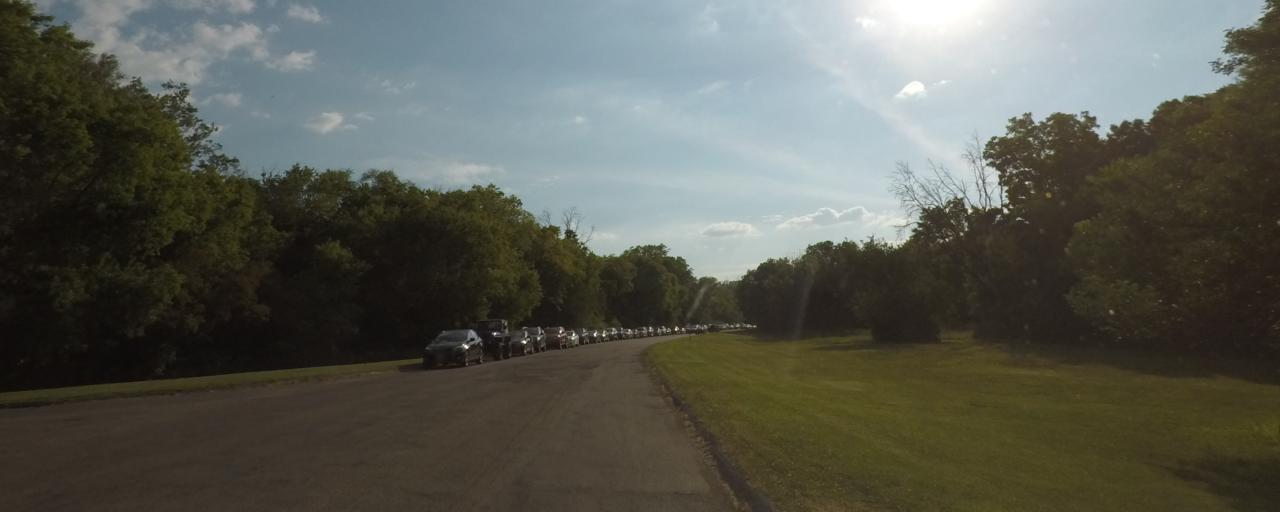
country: US
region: Wisconsin
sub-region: Milwaukee County
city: Hales Corners
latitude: 42.9309
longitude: -88.0242
